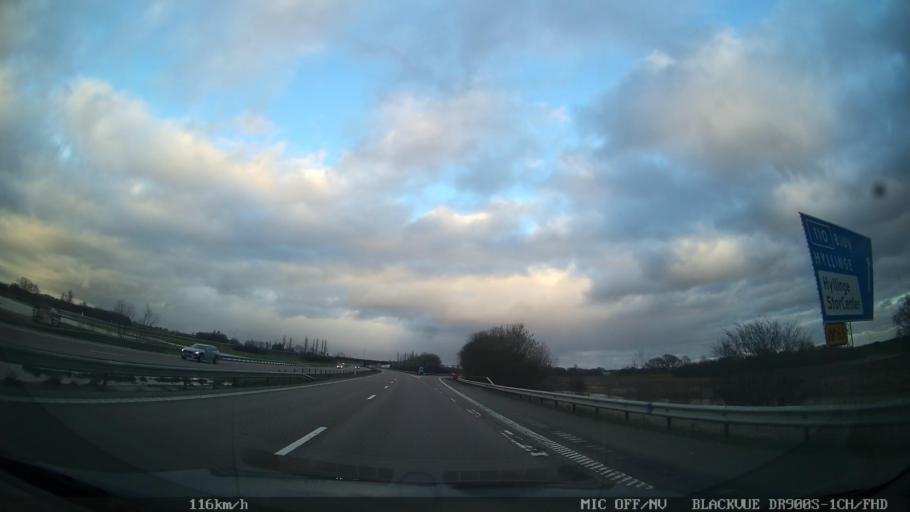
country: SE
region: Skane
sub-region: Helsingborg
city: Hyllinge
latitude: 56.0992
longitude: 12.8412
